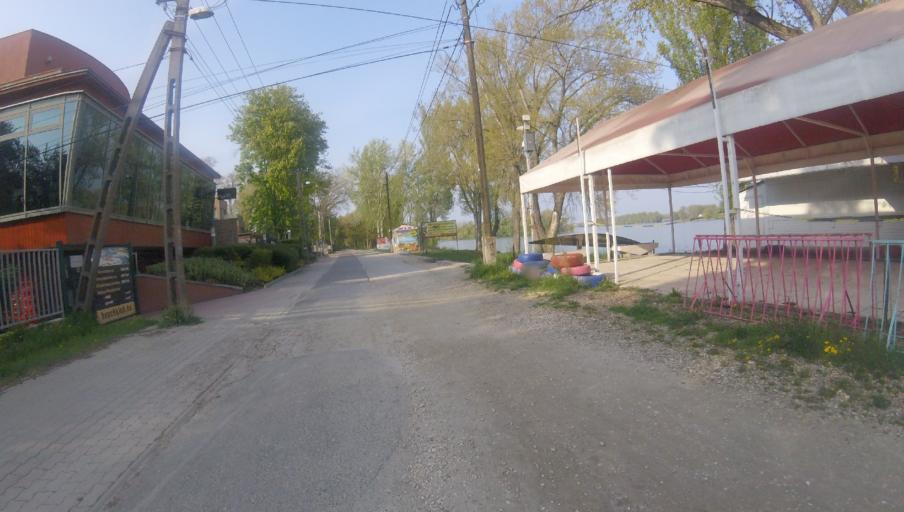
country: HU
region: Budapest
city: Budapest IV. keruelet
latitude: 47.5872
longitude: 19.0684
